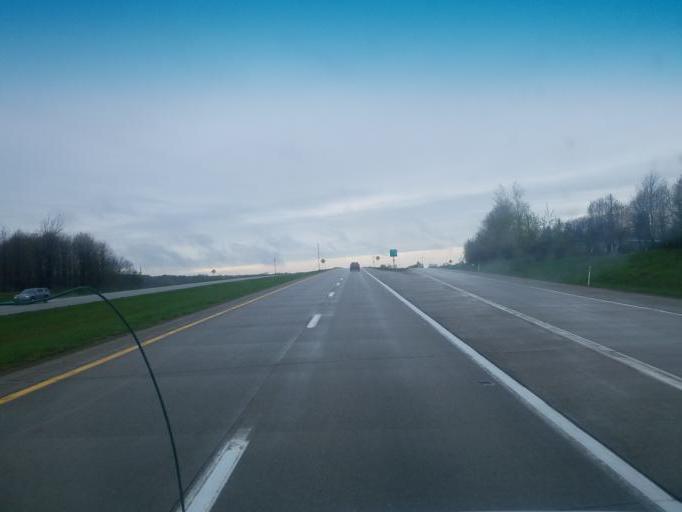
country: US
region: Pennsylvania
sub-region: Erie County
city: North East
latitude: 42.1360
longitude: -79.8182
